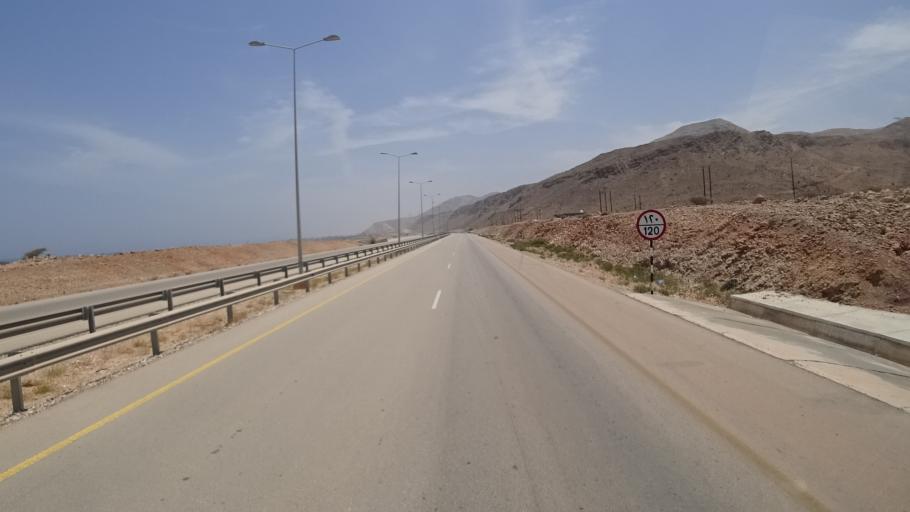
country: OM
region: Ash Sharqiyah
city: Sur
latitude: 22.7254
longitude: 59.3451
